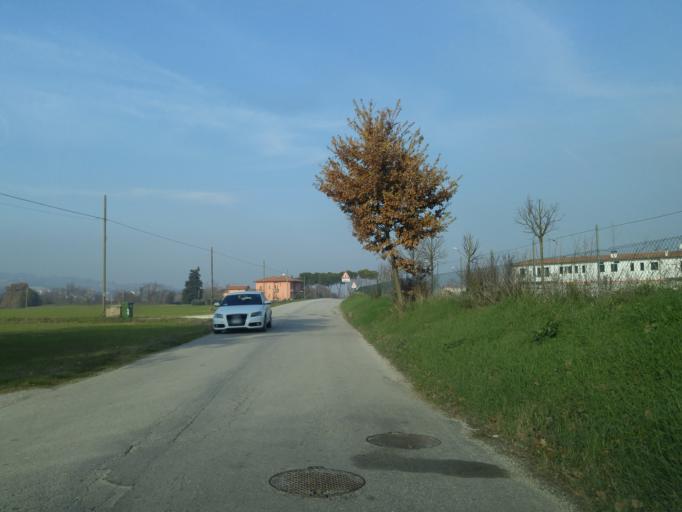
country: IT
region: The Marches
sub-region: Provincia di Pesaro e Urbino
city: Villanova
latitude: 43.7326
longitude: 12.9215
